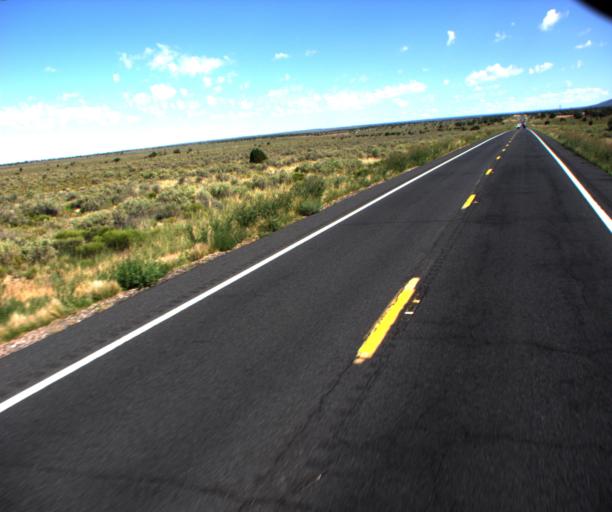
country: US
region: Arizona
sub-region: Coconino County
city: Grand Canyon Village
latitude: 35.6930
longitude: -112.1339
